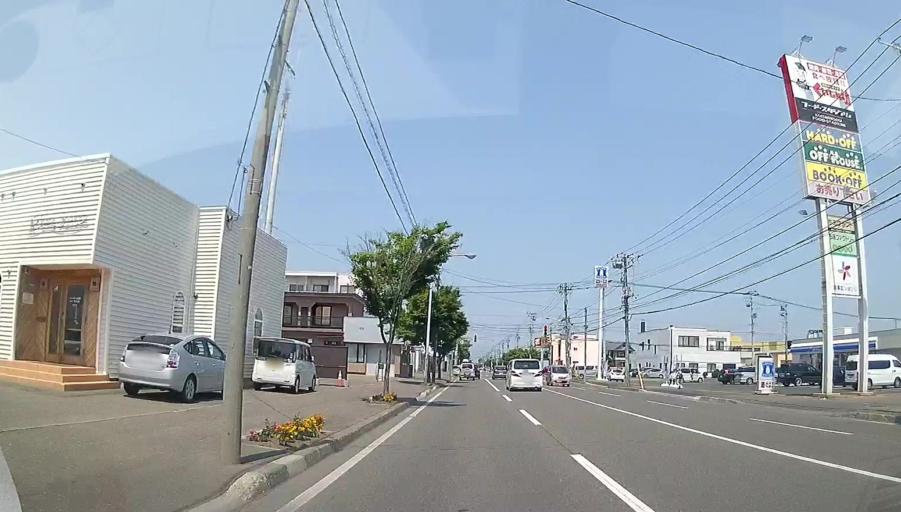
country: JP
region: Hokkaido
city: Obihiro
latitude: 42.8960
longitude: 143.2008
